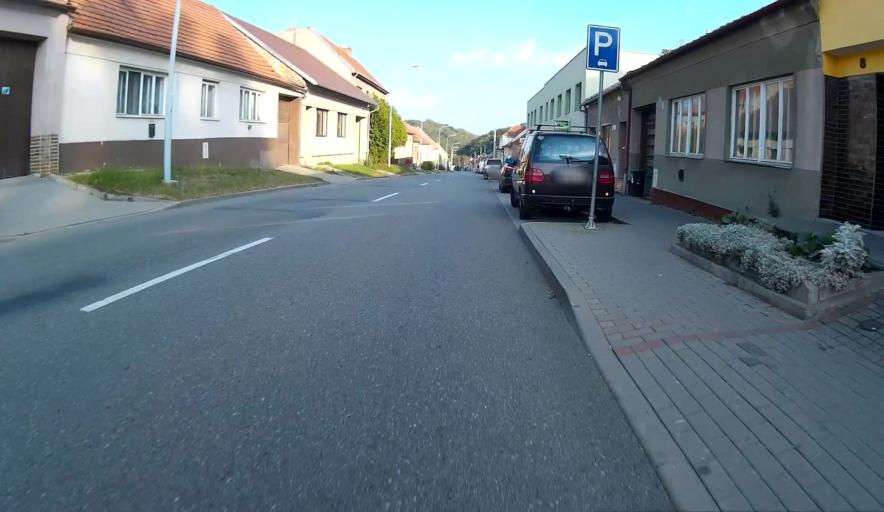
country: CZ
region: South Moravian
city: Podoli
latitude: 49.2069
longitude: 16.6963
